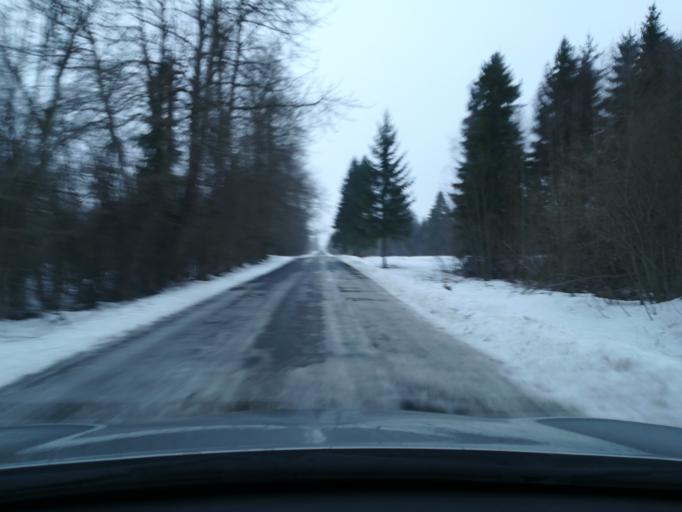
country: EE
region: Harju
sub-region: Raasiku vald
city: Raasiku
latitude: 59.3468
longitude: 25.2161
